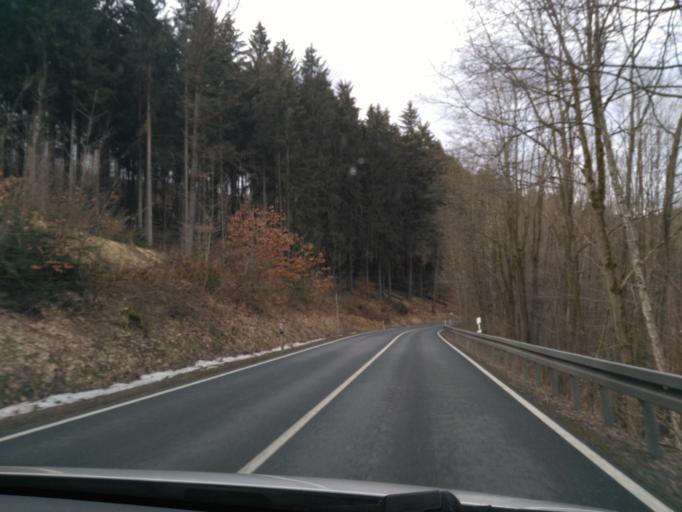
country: DE
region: Saxony
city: Wolkenstein
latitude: 50.6648
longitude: 13.0589
